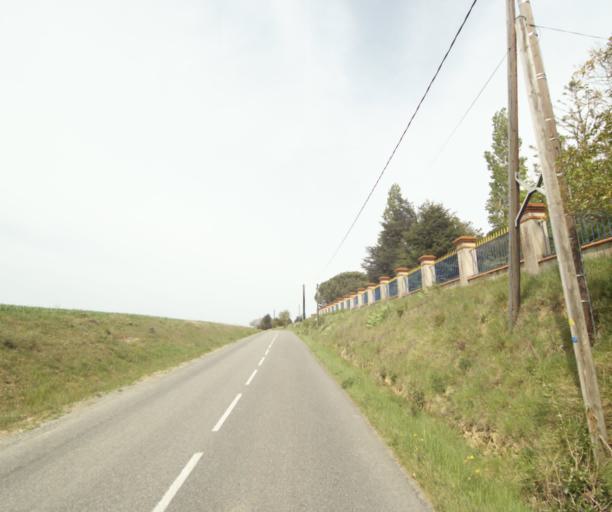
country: FR
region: Midi-Pyrenees
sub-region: Departement de la Haute-Garonne
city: Pechabou
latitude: 43.4897
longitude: 1.4987
